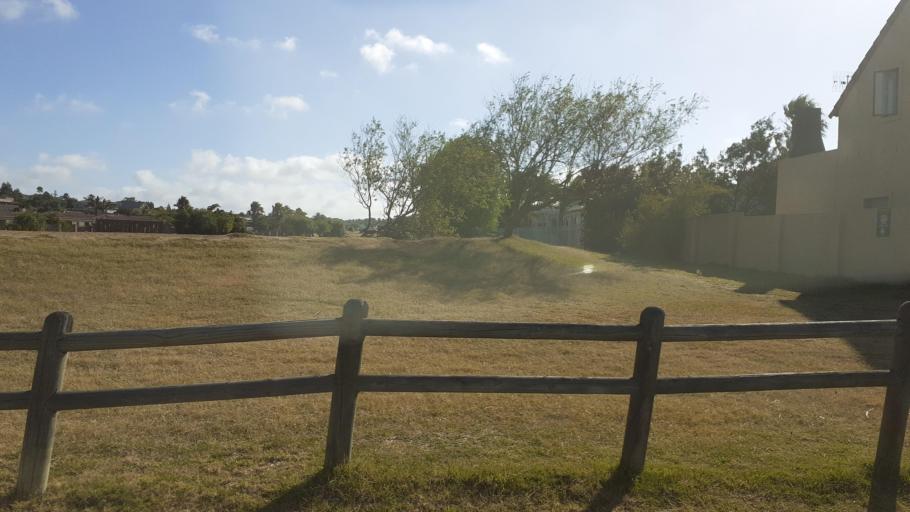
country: ZA
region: Western Cape
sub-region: City of Cape Town
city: Kraaifontein
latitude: -33.8146
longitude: 18.6906
